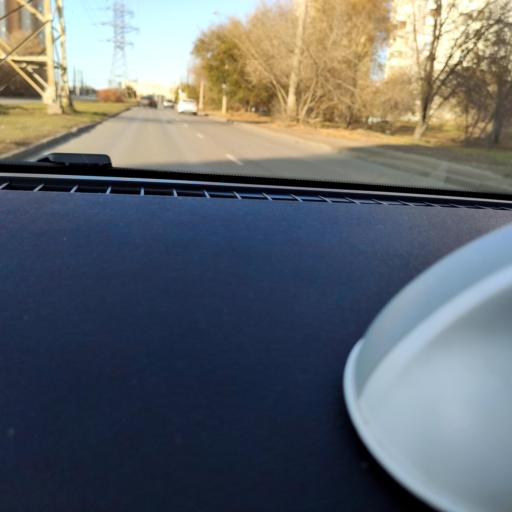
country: RU
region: Samara
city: Samara
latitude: 53.2096
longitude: 50.2133
